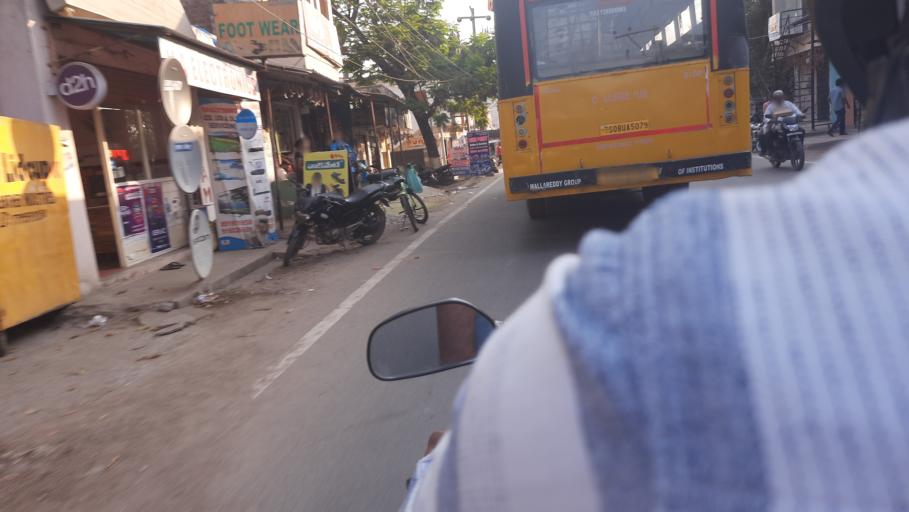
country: IN
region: Telangana
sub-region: Rangareddi
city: Secunderabad
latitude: 17.5053
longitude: 78.5405
